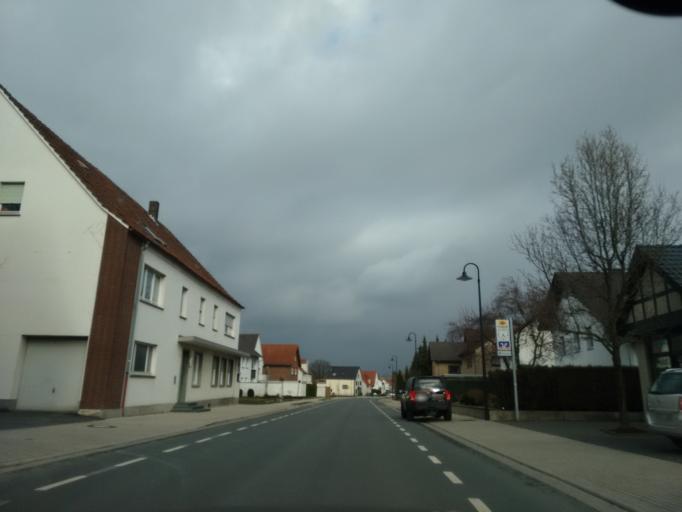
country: DE
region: North Rhine-Westphalia
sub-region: Regierungsbezirk Detmold
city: Salzkotten
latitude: 51.6833
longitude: 8.5676
